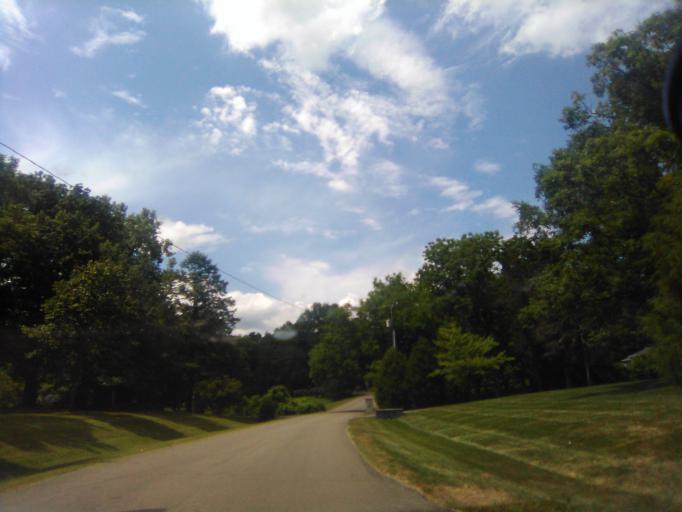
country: US
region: Tennessee
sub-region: Davidson County
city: Belle Meade
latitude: 36.1244
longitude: -86.8785
